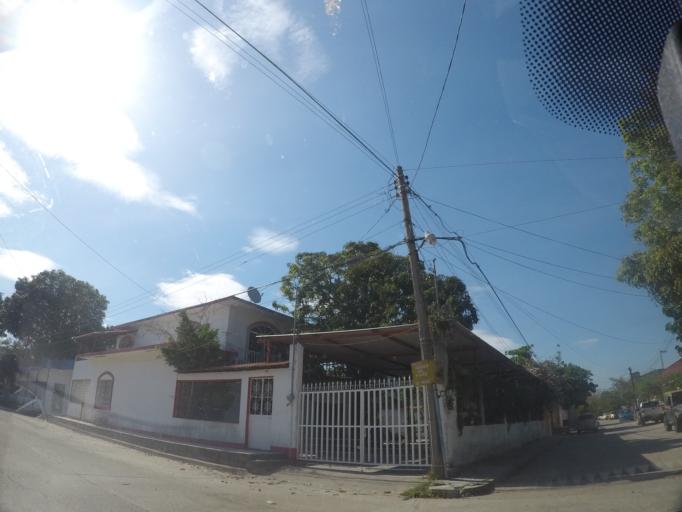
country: MX
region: Oaxaca
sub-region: Salina Cruz
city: Salina Cruz
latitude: 16.2137
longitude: -95.1937
